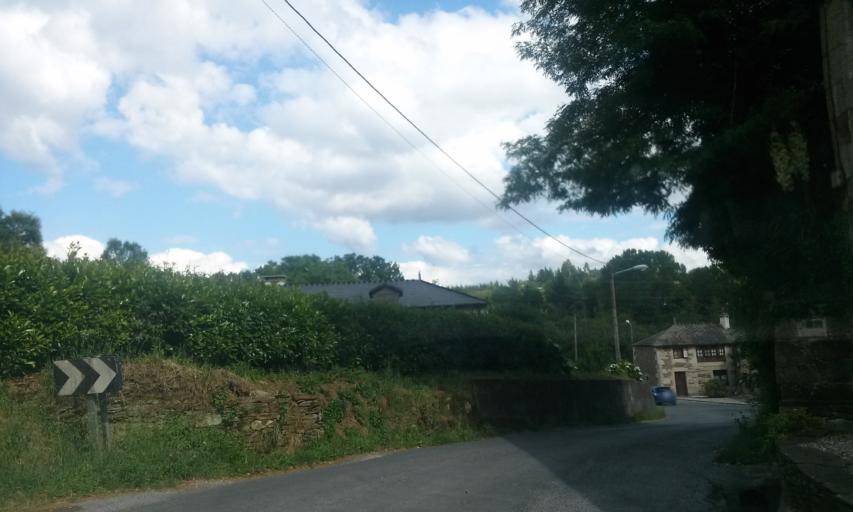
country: ES
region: Galicia
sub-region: Provincia de Lugo
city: Rabade
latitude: 43.1171
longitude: -7.6585
